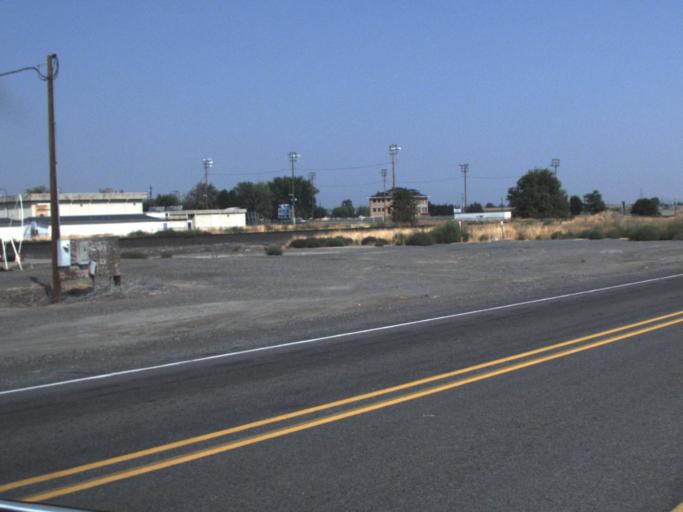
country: US
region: Washington
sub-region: Yakima County
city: Mabton
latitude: 46.2109
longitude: -119.9977
